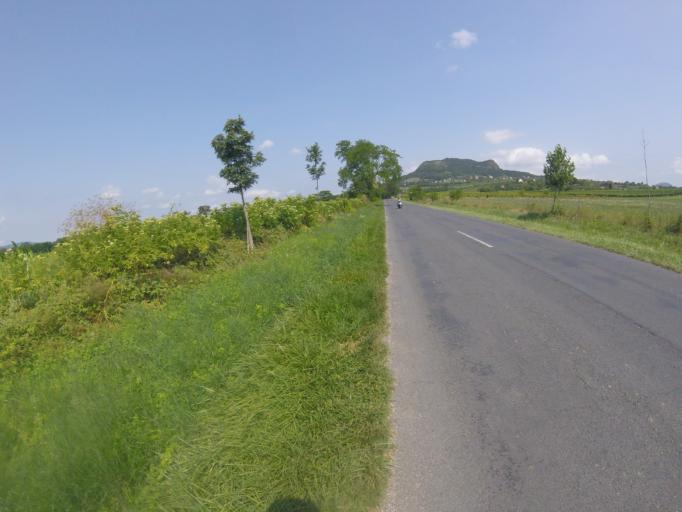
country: HU
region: Veszprem
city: Tapolca
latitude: 46.8223
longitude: 17.4474
